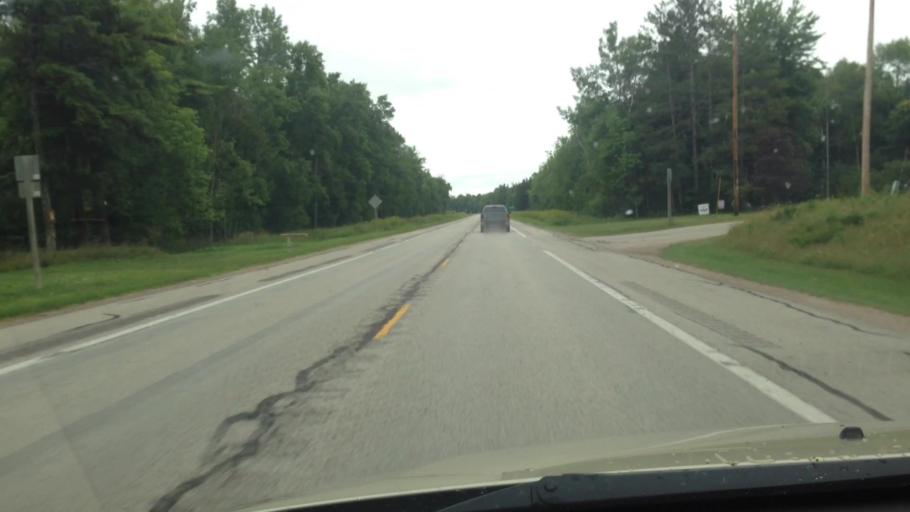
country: US
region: Michigan
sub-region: Delta County
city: Escanaba
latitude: 45.5795
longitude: -87.2448
